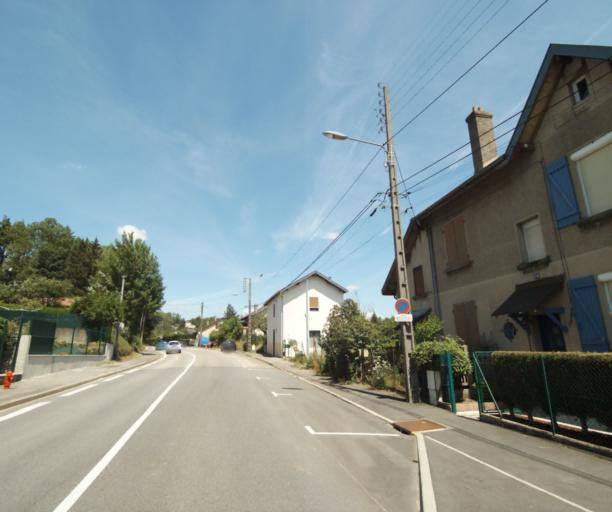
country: FR
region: Lorraine
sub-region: Departement de Meurthe-et-Moselle
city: Luneville
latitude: 48.6042
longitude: 6.4876
